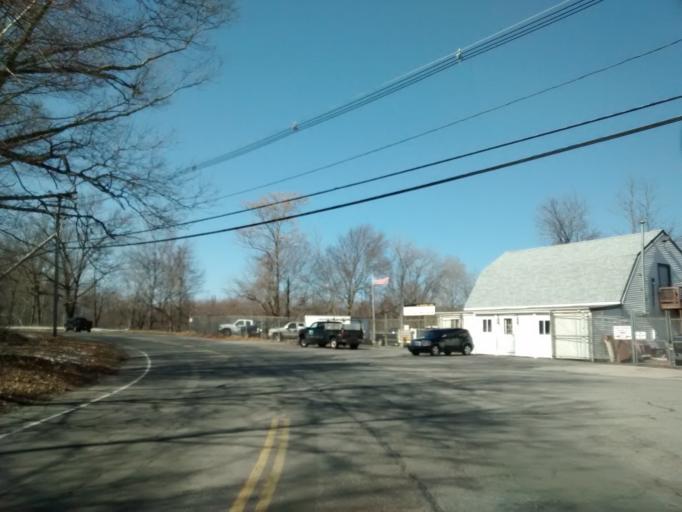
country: US
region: Massachusetts
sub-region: Worcester County
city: Millbury
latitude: 42.1808
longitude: -71.7335
